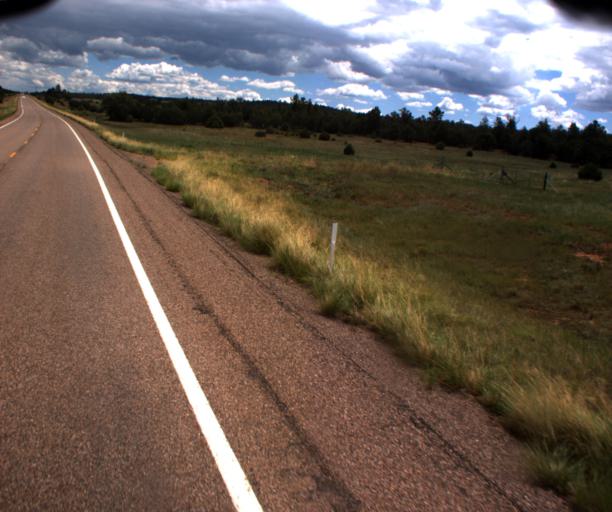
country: US
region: Arizona
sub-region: Navajo County
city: Linden
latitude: 34.3486
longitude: -110.3059
